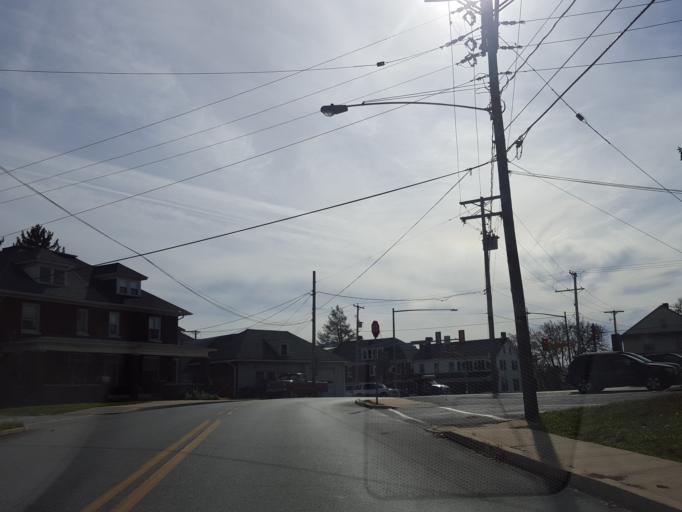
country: US
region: Pennsylvania
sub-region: York County
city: Red Lion
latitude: 39.9069
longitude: -76.6111
